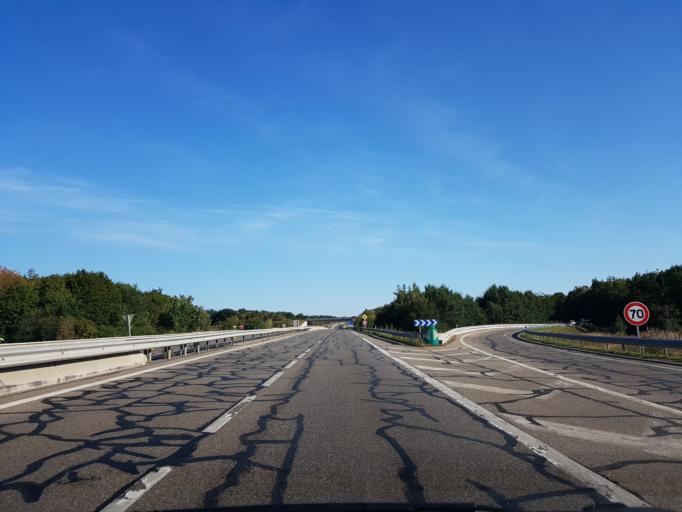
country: FR
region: Alsace
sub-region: Departement du Haut-Rhin
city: Pulversheim
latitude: 47.8219
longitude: 7.2905
